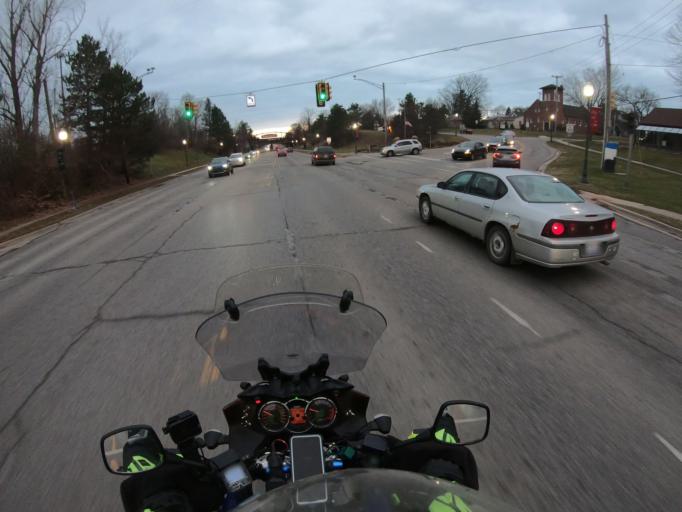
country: US
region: Michigan
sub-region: Genesee County
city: Grand Blanc
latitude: 42.9311
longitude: -83.6341
